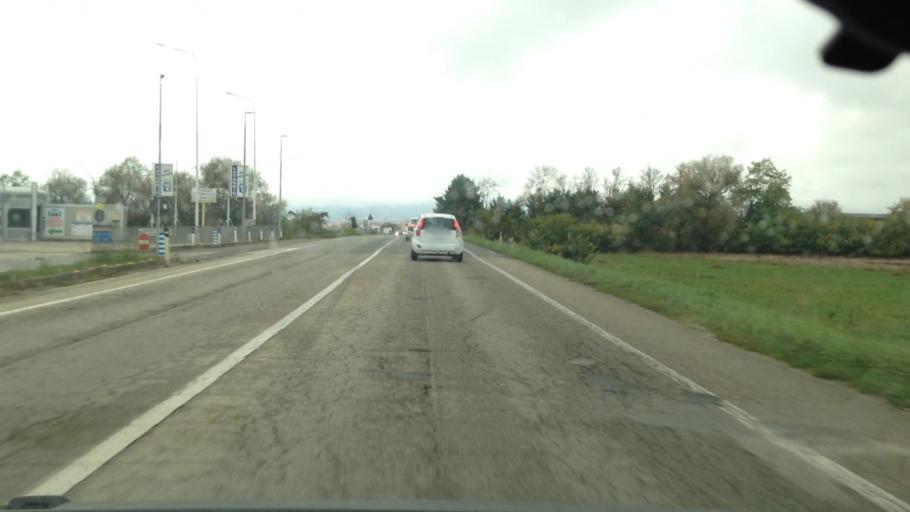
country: IT
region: Piedmont
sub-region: Provincia di Torino
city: Riva Presso Chieri
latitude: 44.9910
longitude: 7.8667
